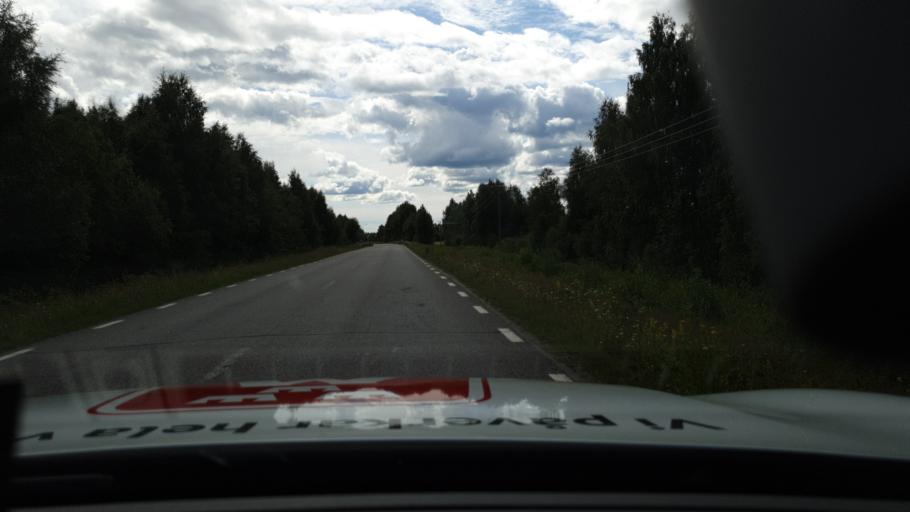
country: SE
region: Norrbotten
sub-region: Bodens Kommun
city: Boden
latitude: 65.8803
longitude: 21.6784
